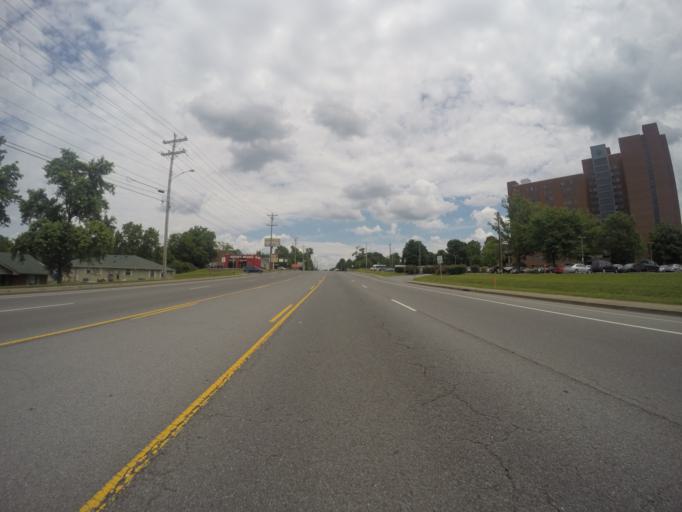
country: US
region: Tennessee
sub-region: Davidson County
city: Lakewood
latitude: 36.2053
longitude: -86.6138
